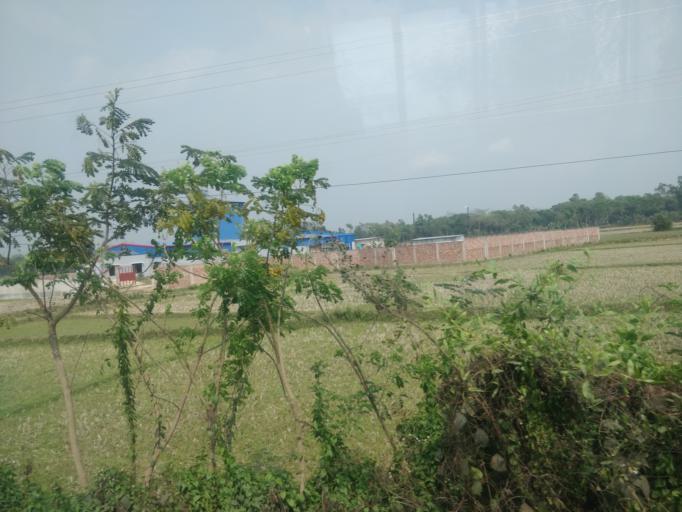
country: BD
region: Sylhet
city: Habiganj
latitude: 24.3176
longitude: 91.4358
